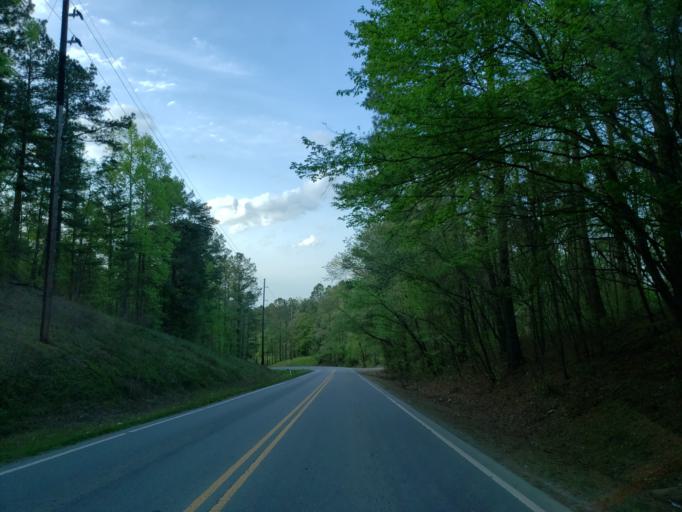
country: US
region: Georgia
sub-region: Cherokee County
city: Ball Ground
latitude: 34.2961
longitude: -84.3948
